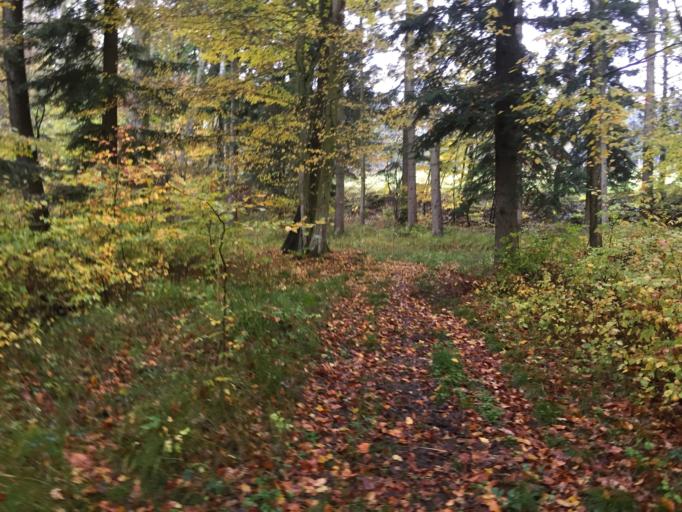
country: AT
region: Styria
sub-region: Politischer Bezirk Graz-Umgebung
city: Hart bei Graz
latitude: 47.0692
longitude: 15.5389
